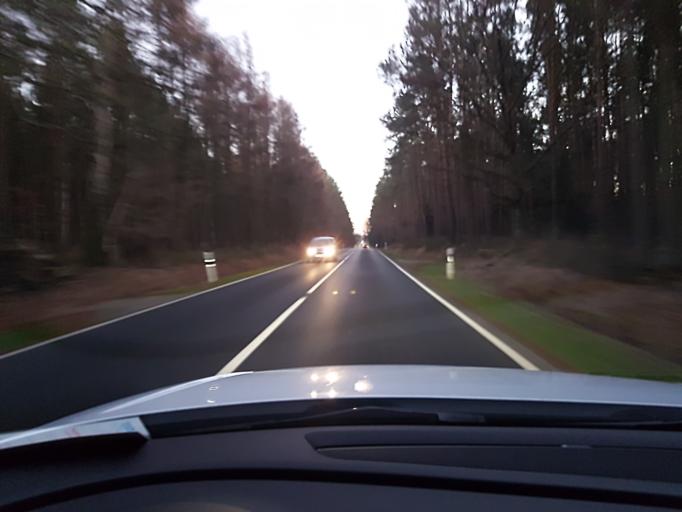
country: DE
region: Mecklenburg-Vorpommern
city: Gingst
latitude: 54.5053
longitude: 13.2770
